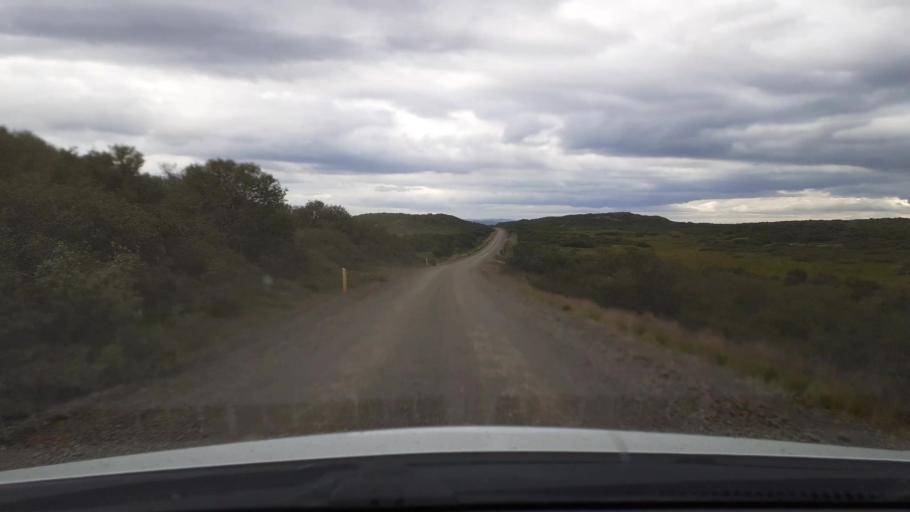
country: IS
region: West
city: Borgarnes
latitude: 64.5975
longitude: -21.9797
